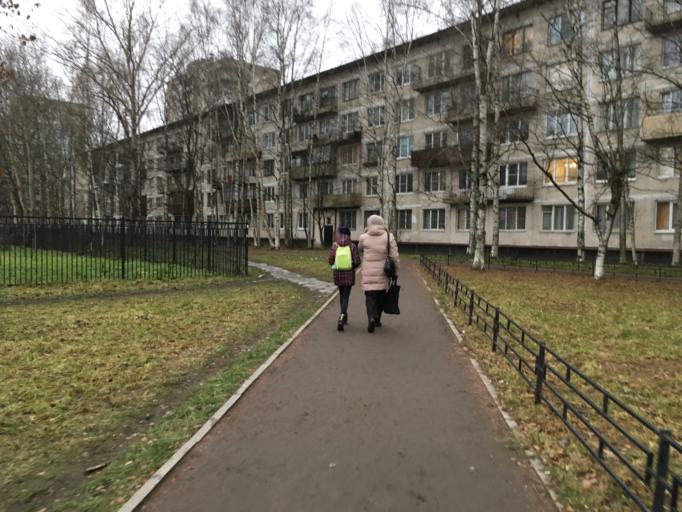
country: RU
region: St.-Petersburg
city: Obukhovo
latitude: 59.9019
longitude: 30.4805
